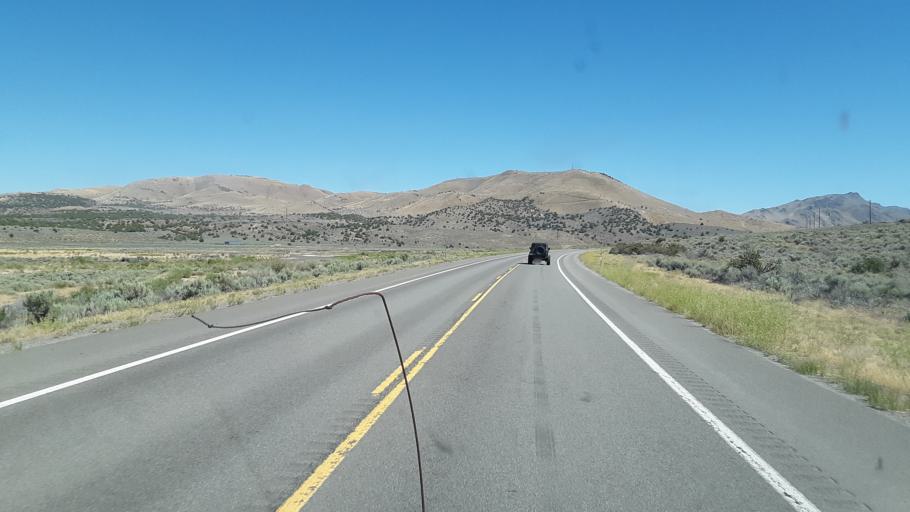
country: US
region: Nevada
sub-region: Washoe County
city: Cold Springs
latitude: 39.9478
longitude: -120.0277
